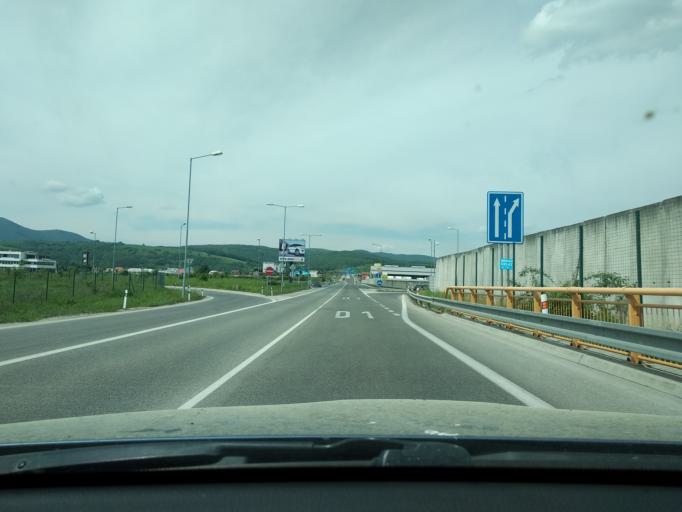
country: SK
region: Trenciansky
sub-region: Okres Trencin
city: Trencin
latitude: 48.8882
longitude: 18.0088
